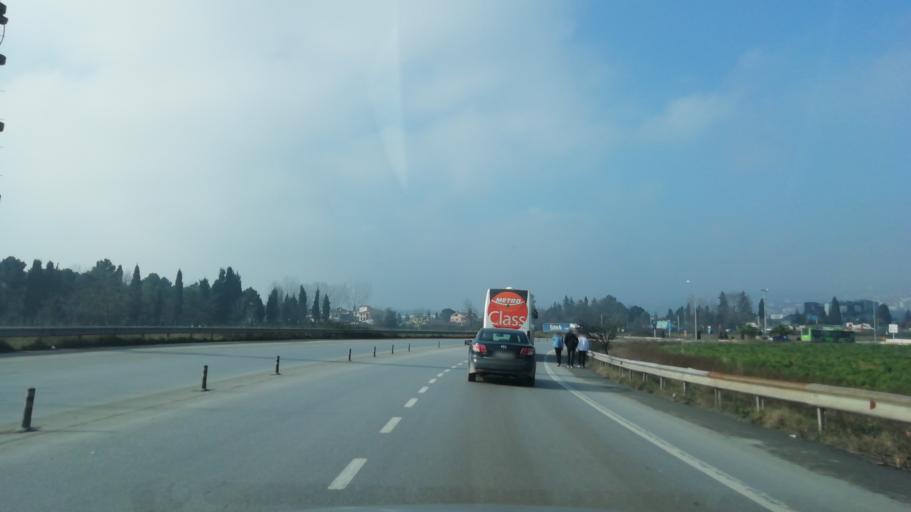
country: TR
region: Sakarya
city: Adapazari
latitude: 40.7273
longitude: 30.3806
